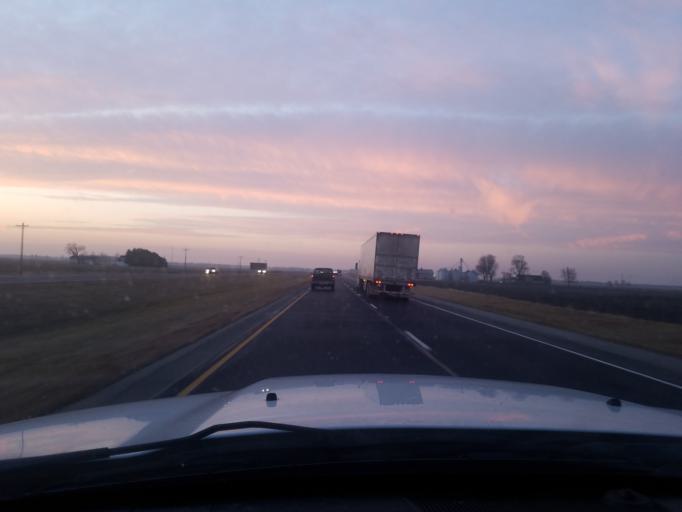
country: US
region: Indiana
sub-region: Huntington County
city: Markle
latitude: 40.8632
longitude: -85.3449
